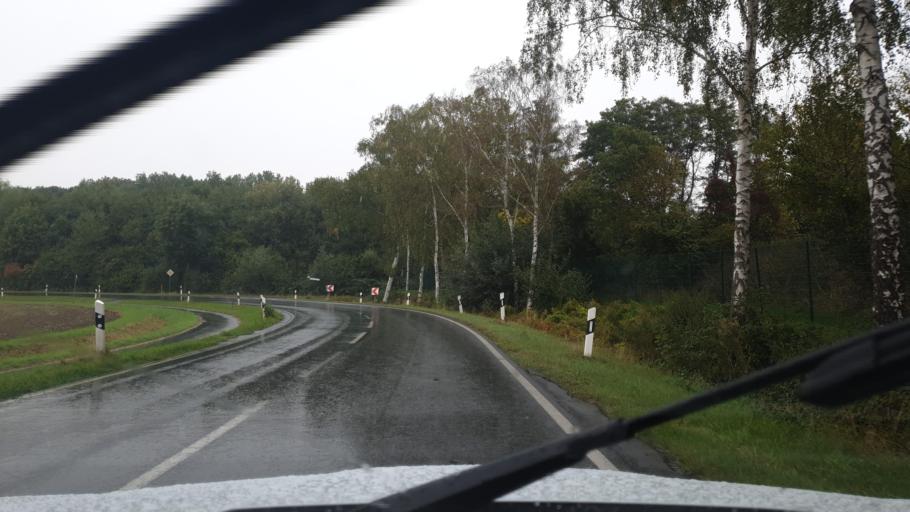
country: DE
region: North Rhine-Westphalia
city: Porta Westfalica
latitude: 52.2076
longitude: 8.8993
